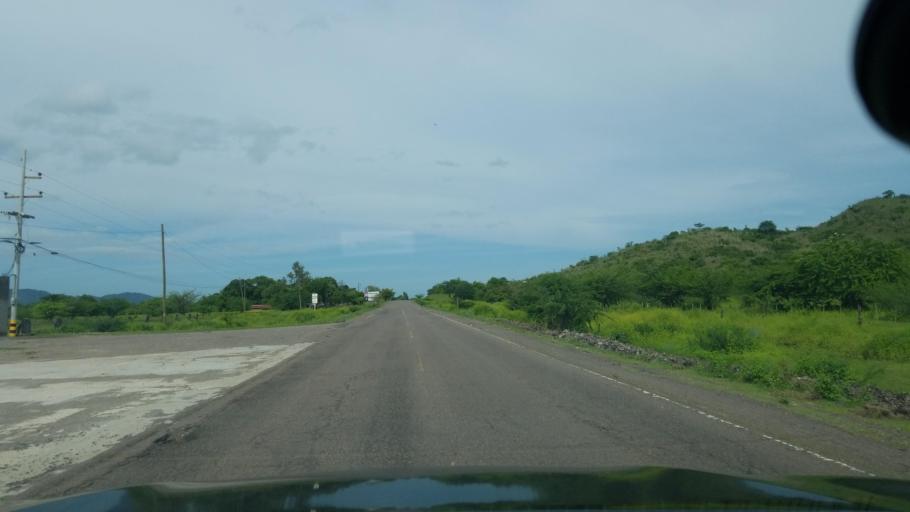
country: HN
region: Choluteca
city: Santa Ana de Yusguare
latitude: 13.3550
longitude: -87.1022
